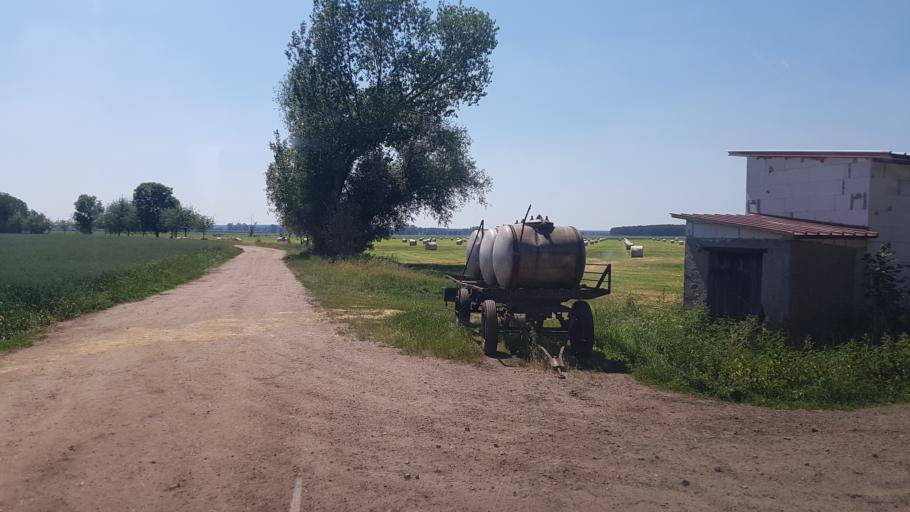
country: DE
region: Brandenburg
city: Schlieben
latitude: 51.7236
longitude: 13.3264
